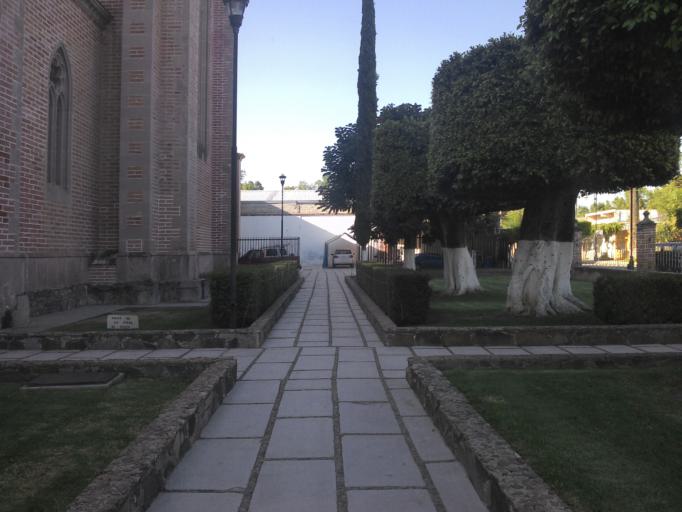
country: MX
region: Jalisco
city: San Diego de Alejandria
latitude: 20.8800
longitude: -101.9819
